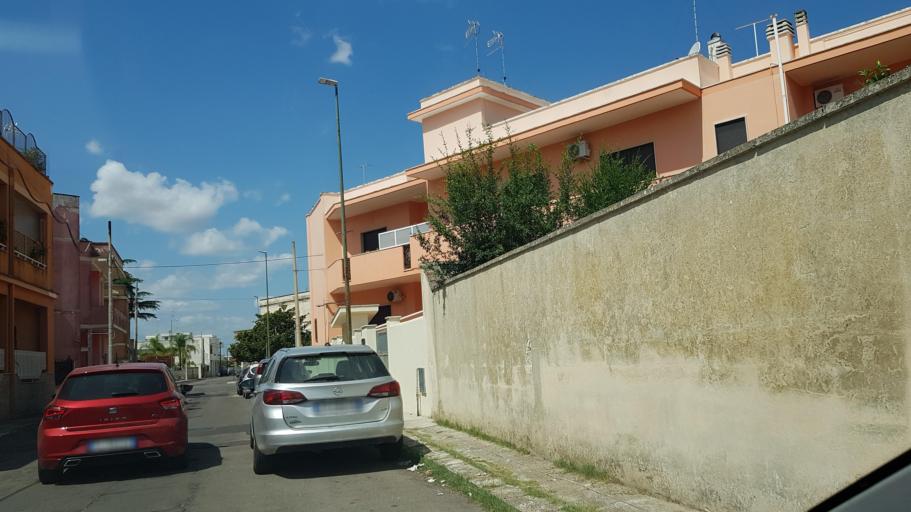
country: IT
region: Apulia
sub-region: Provincia di Lecce
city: Trepuzzi
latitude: 40.4078
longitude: 18.0647
